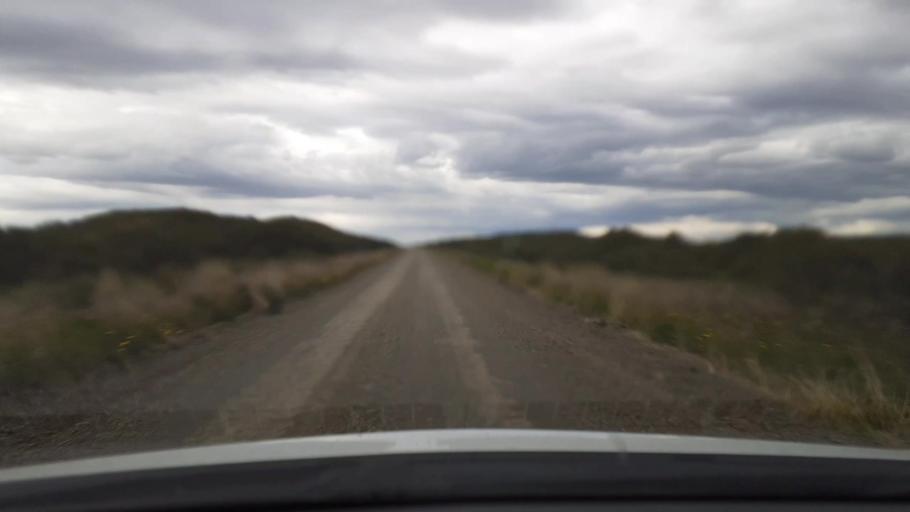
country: IS
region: West
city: Borgarnes
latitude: 64.5998
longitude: -21.9756
